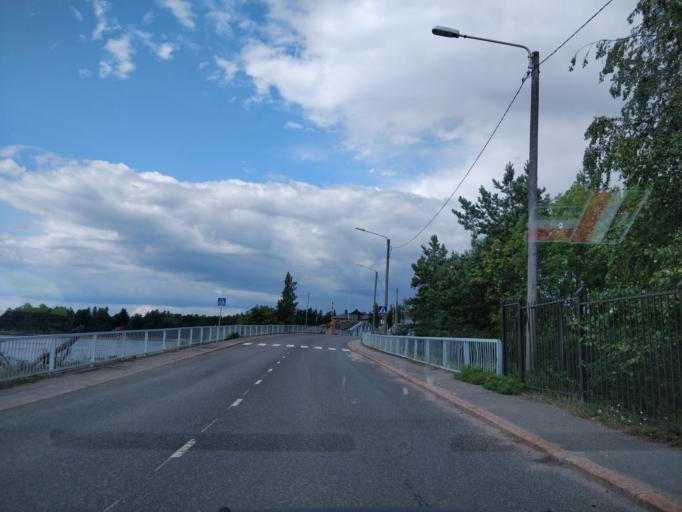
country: FI
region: Uusimaa
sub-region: Helsinki
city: Helsinki
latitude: 60.1567
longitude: 25.0498
